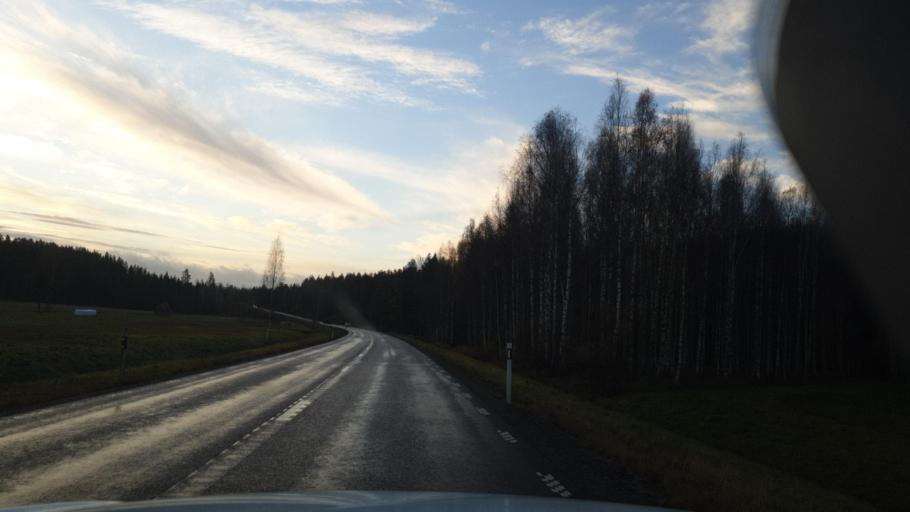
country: SE
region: Vaermland
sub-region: Arvika Kommun
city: Arvika
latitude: 59.5553
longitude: 12.7253
